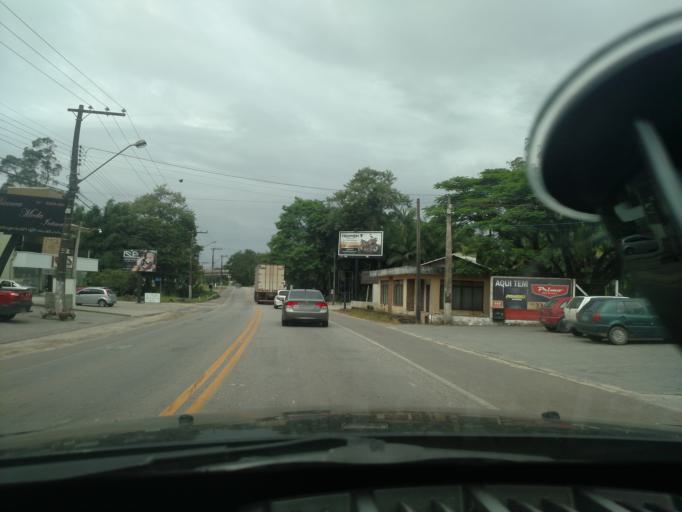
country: BR
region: Santa Catarina
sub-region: Gaspar
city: Gaspar
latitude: -26.8924
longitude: -48.8211
